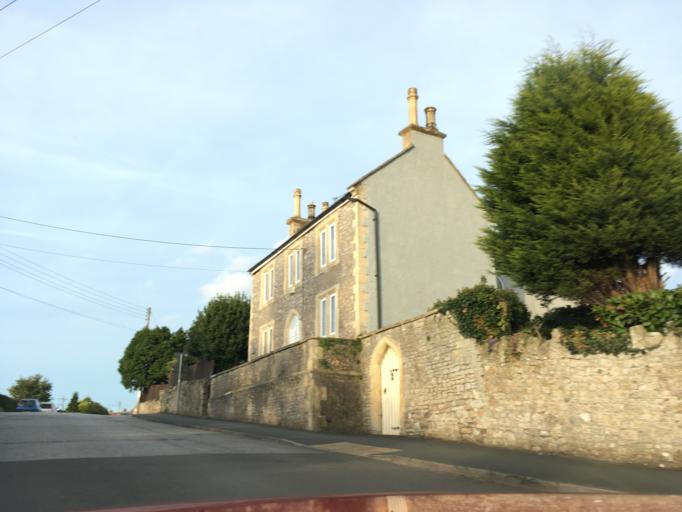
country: GB
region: England
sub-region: South Gloucestershire
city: Almondsbury
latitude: 51.5841
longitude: -2.5775
